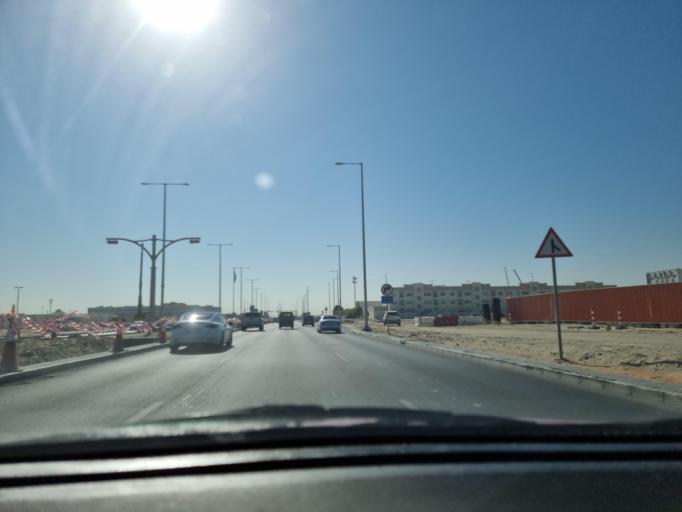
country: AE
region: Abu Dhabi
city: Abu Dhabi
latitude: 24.4172
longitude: 54.5675
